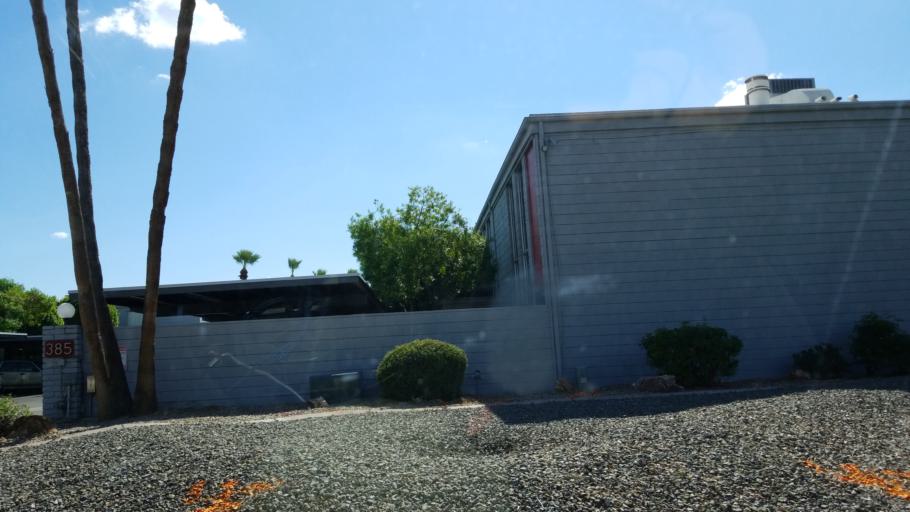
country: US
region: Arizona
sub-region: Maricopa County
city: Phoenix
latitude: 33.5075
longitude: -112.0806
